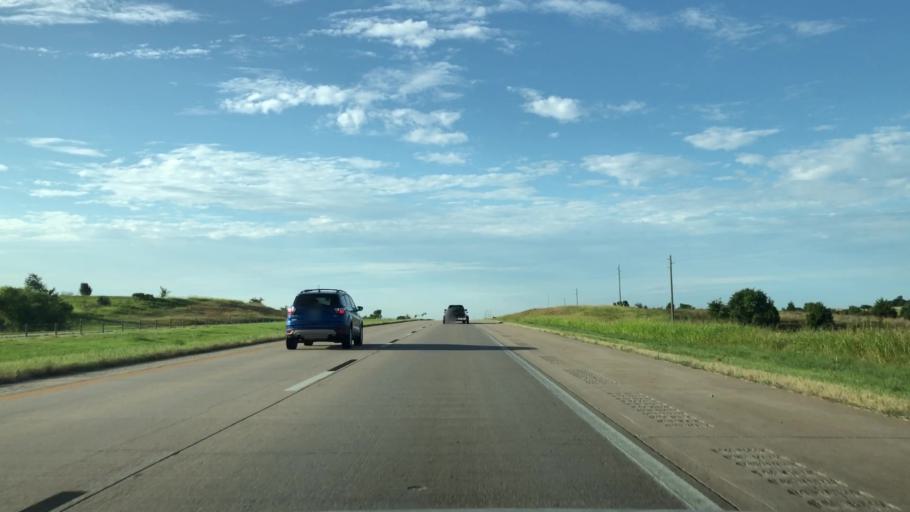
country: US
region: Oklahoma
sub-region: Osage County
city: Skiatook
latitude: 36.5220
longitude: -95.9255
